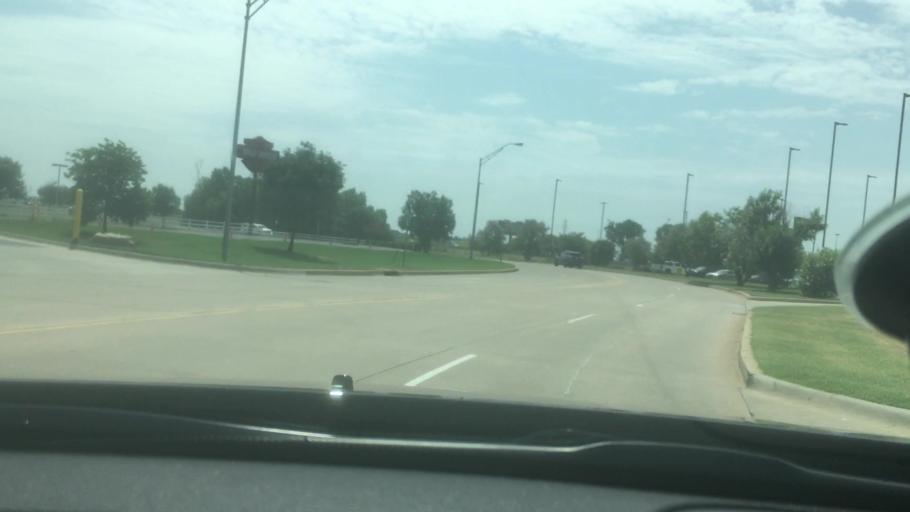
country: US
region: Oklahoma
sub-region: Oklahoma County
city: Bethany
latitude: 35.4625
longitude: -97.6347
